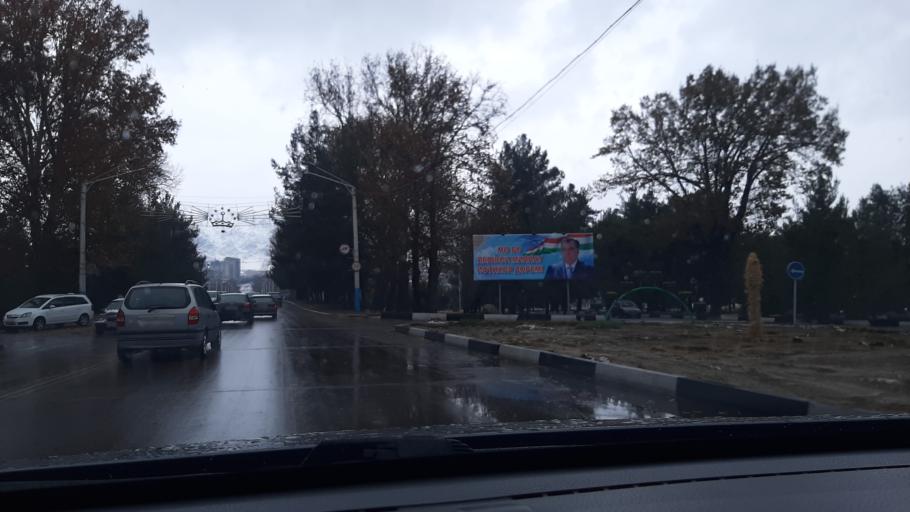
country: TJ
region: Viloyati Sughd
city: Khujand
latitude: 40.2879
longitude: 69.6217
